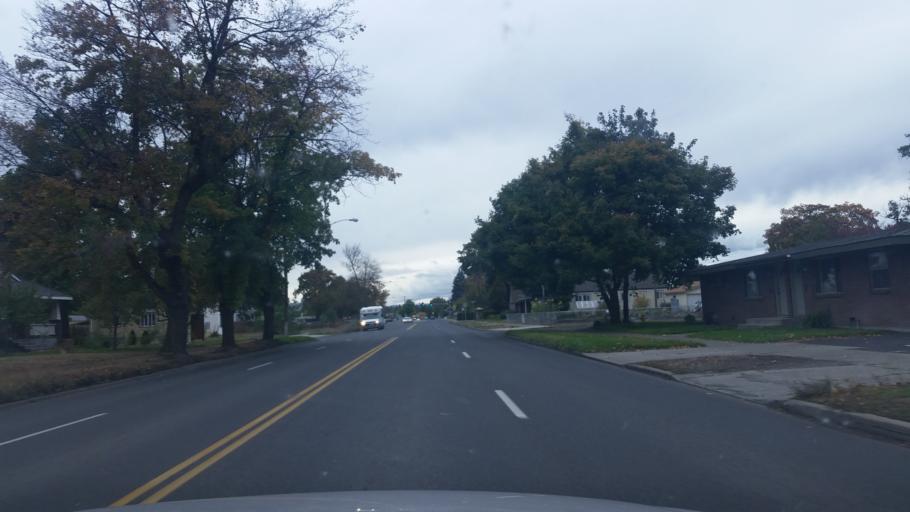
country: US
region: Washington
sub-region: Spokane County
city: Spokane
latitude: 47.6719
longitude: -117.3773
